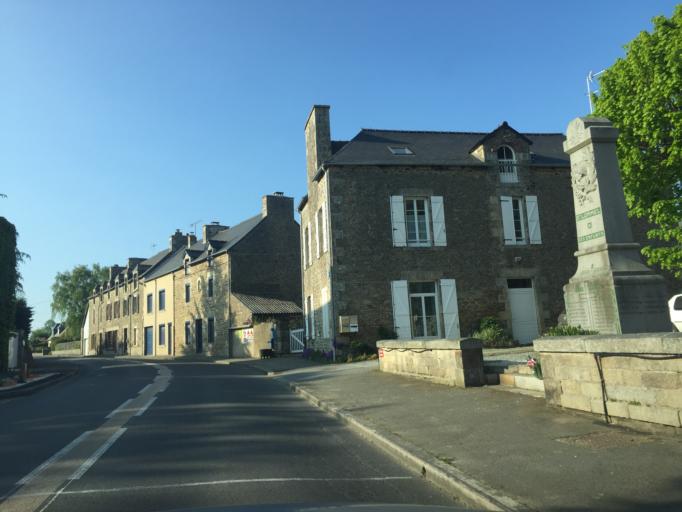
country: FR
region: Brittany
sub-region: Departement des Cotes-d'Armor
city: Crehen
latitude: 48.5457
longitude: -2.2296
